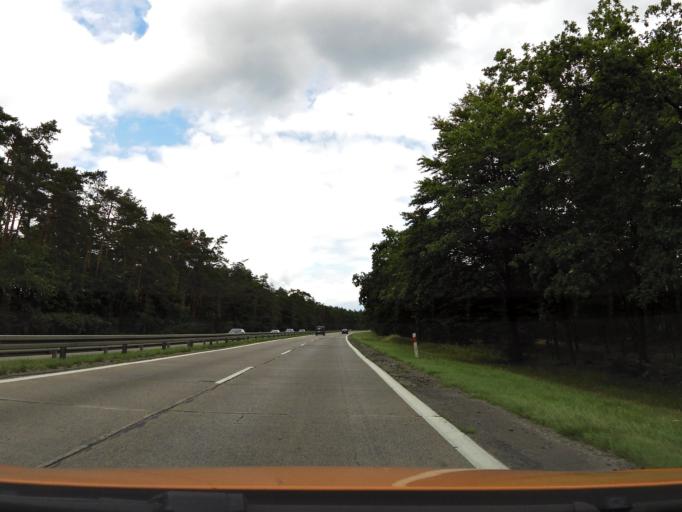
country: PL
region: West Pomeranian Voivodeship
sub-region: Powiat gryfinski
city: Stare Czarnowo
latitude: 53.4104
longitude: 14.7310
